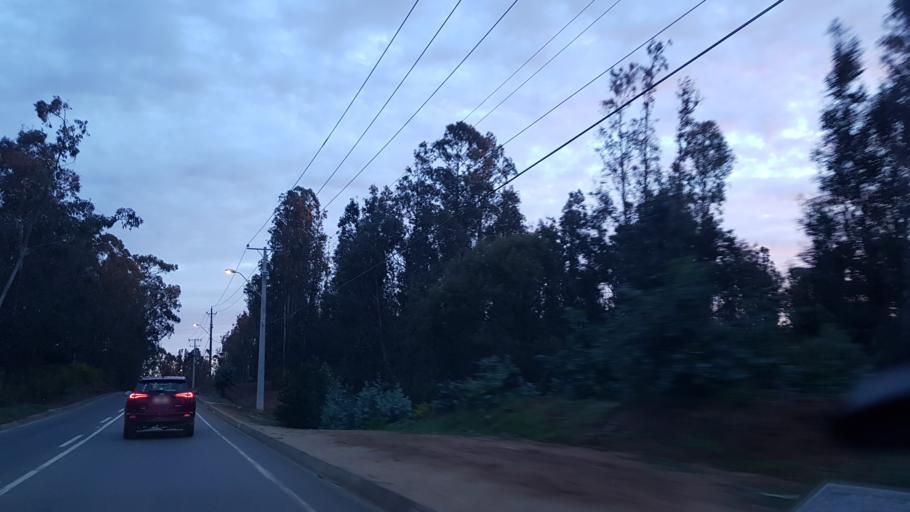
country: CL
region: Valparaiso
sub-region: Provincia de Valparaiso
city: Valparaiso
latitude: -33.0687
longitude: -71.6386
